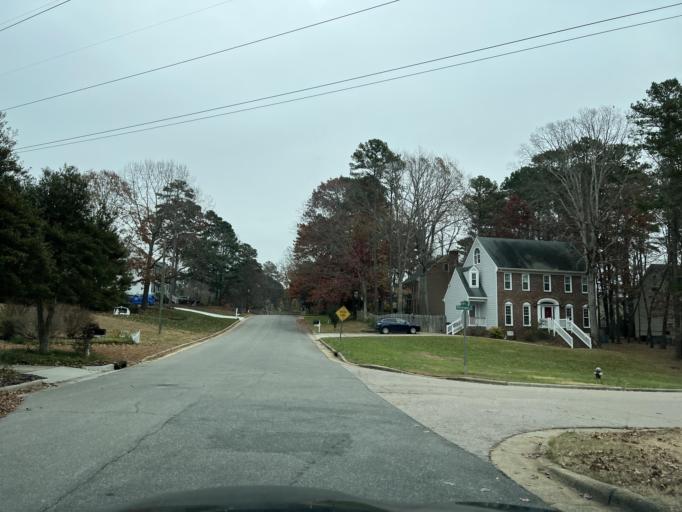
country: US
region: North Carolina
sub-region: Wake County
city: Wake Forest
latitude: 35.8976
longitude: -78.6013
